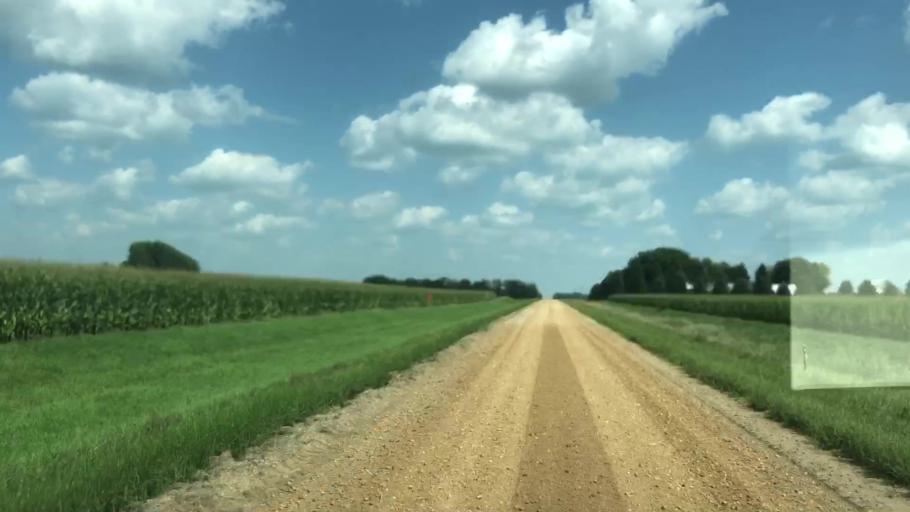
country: US
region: Iowa
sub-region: O'Brien County
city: Sheldon
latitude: 43.1568
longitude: -95.7954
